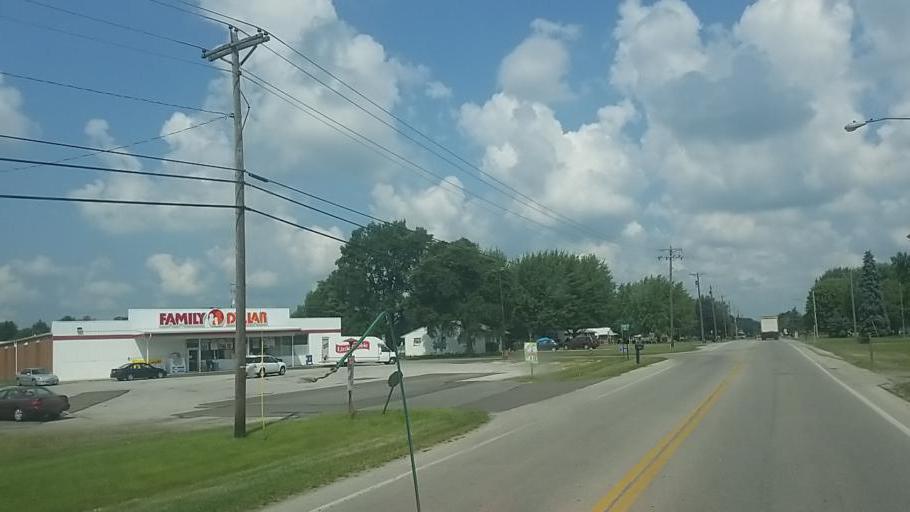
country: US
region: Ohio
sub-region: Wyandot County
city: Upper Sandusky
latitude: 40.8367
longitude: -83.2908
